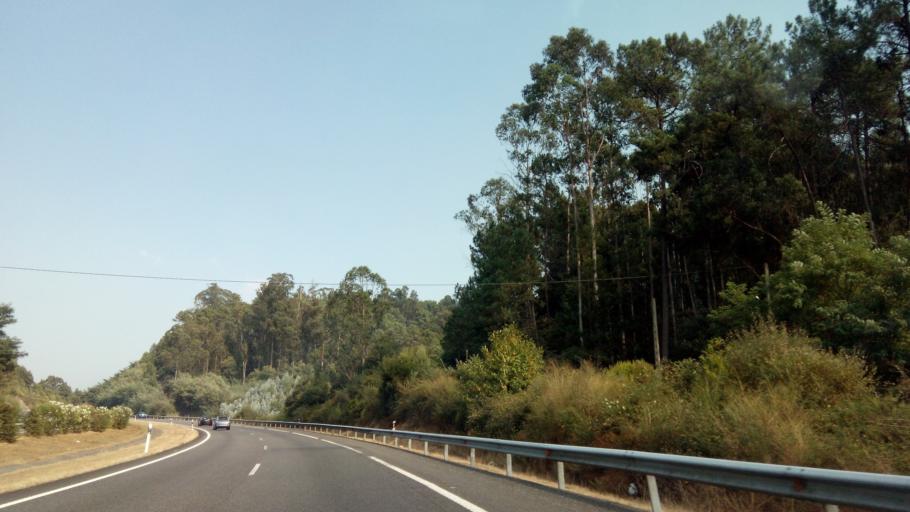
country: ES
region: Galicia
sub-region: Provincia de Pontevedra
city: Ponteareas
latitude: 42.1715
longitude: -8.5522
